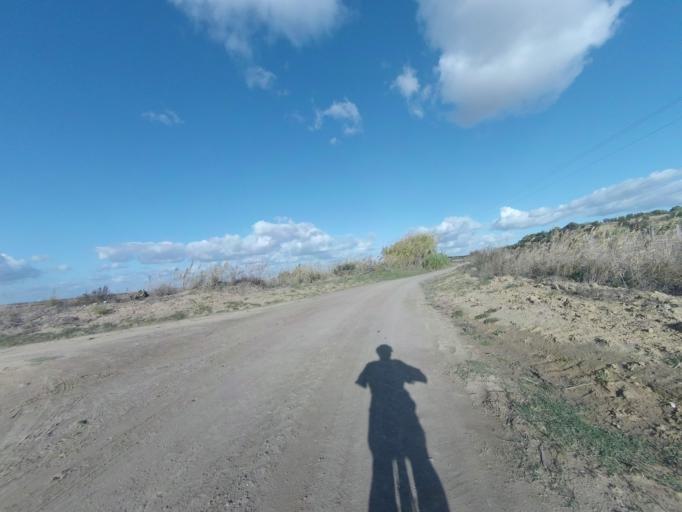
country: ES
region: Andalusia
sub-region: Provincia de Huelva
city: Moguer
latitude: 37.2634
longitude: -6.8691
